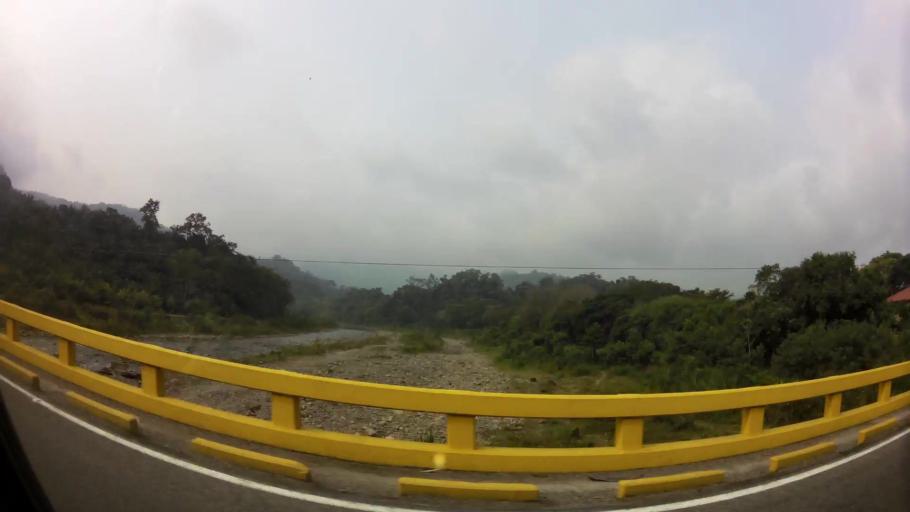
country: HN
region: Yoro
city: Toyos
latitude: 15.5138
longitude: -87.6682
